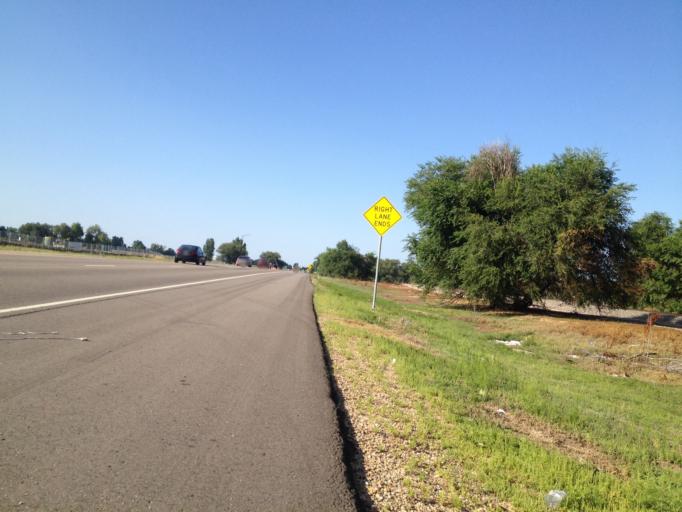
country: US
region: Colorado
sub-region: Boulder County
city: Boulder
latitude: 40.0414
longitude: -105.2414
